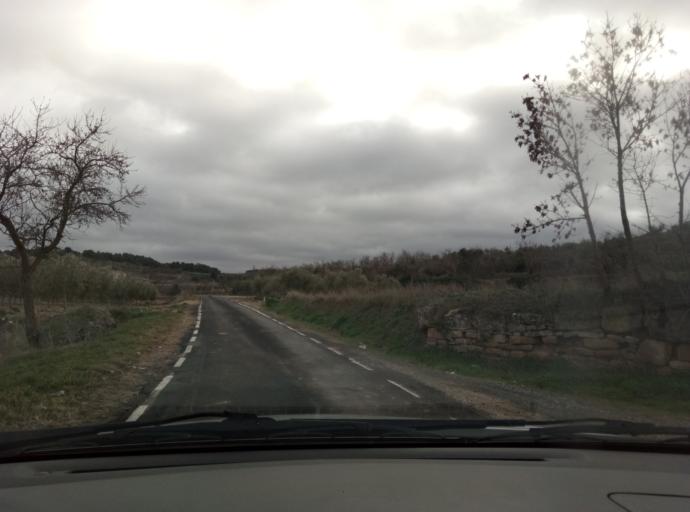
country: ES
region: Catalonia
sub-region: Provincia de Lleida
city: Vallbona de les Monges
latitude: 41.5569
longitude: 1.0666
